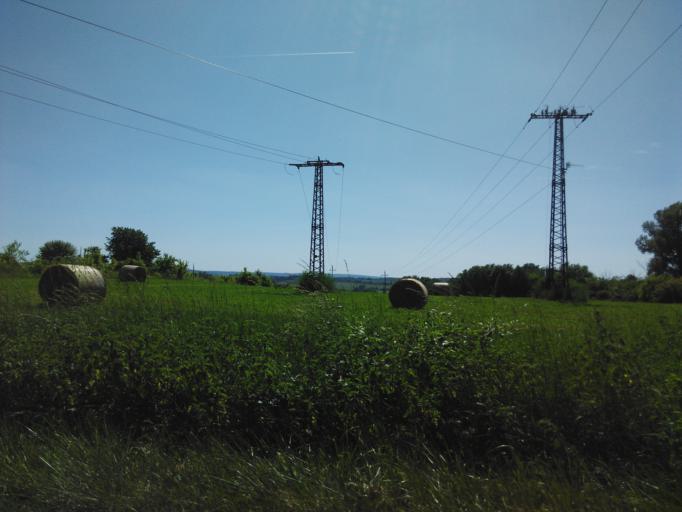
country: HU
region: Fejer
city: Mor
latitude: 47.3597
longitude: 18.2162
